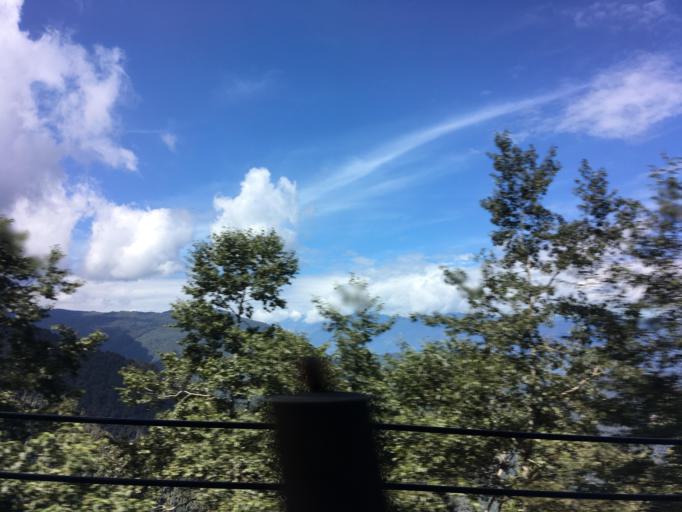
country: TW
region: Taiwan
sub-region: Yilan
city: Yilan
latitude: 24.5084
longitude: 121.5247
